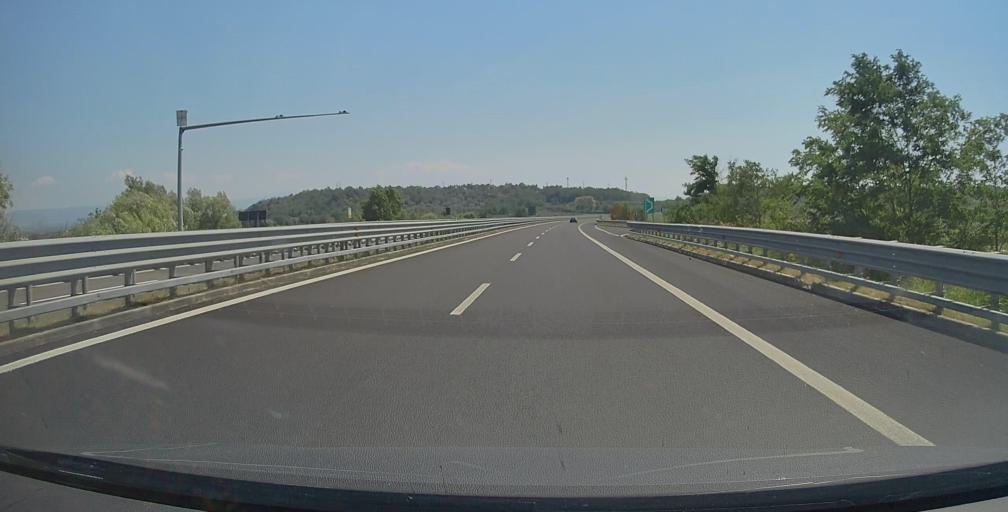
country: IT
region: Calabria
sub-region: Provincia di Reggio Calabria
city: Rosarno
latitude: 38.4912
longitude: 16.0094
